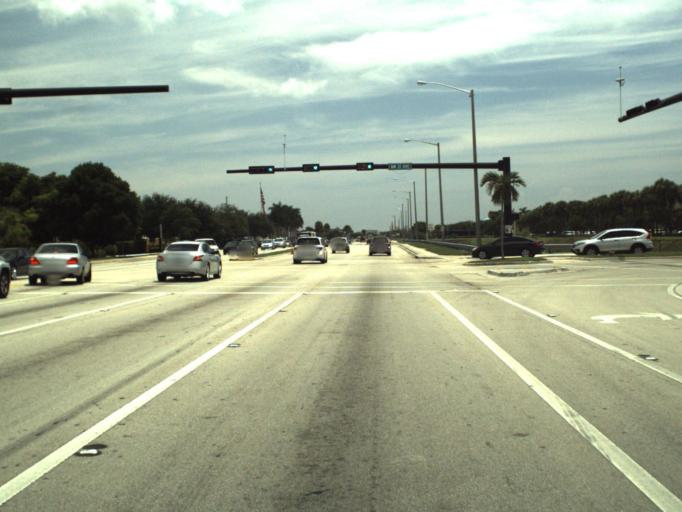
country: US
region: Florida
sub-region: Broward County
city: Pompano Beach
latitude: 26.2313
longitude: -80.1518
